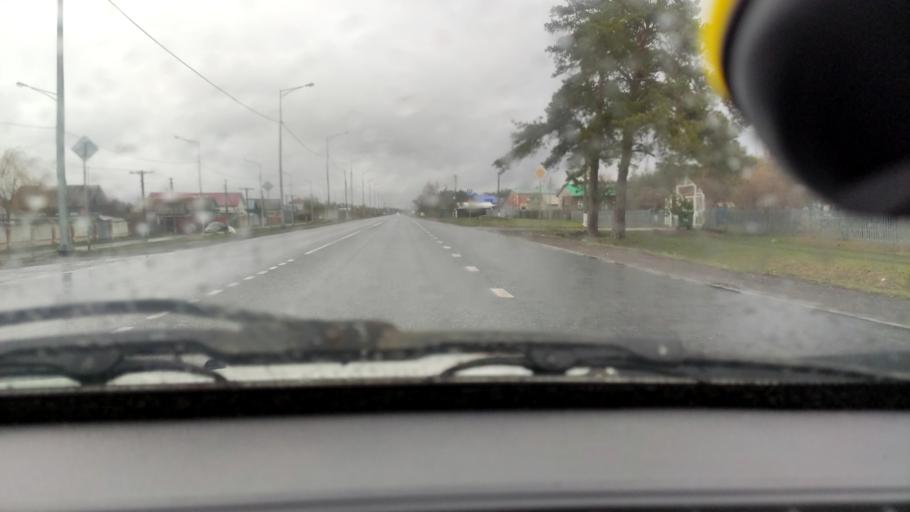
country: RU
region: Samara
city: Povolzhskiy
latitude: 53.5865
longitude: 49.5732
